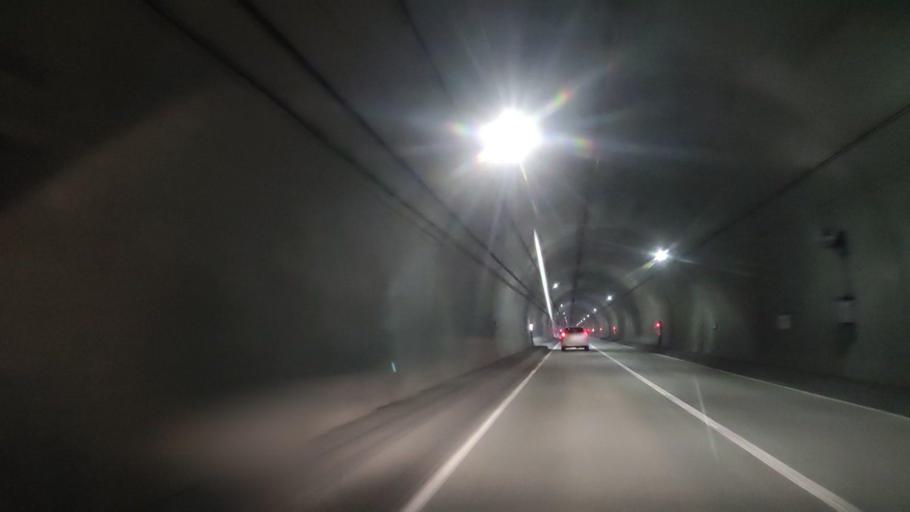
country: JP
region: Hokkaido
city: Rumoi
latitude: 43.7168
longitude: 141.3295
